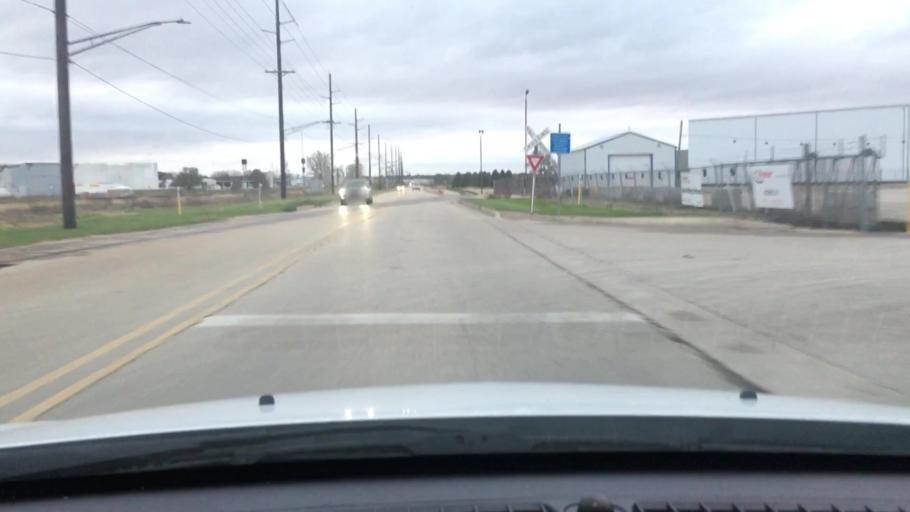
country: US
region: Illinois
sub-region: Ogle County
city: Rochelle
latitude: 41.9091
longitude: -89.0473
